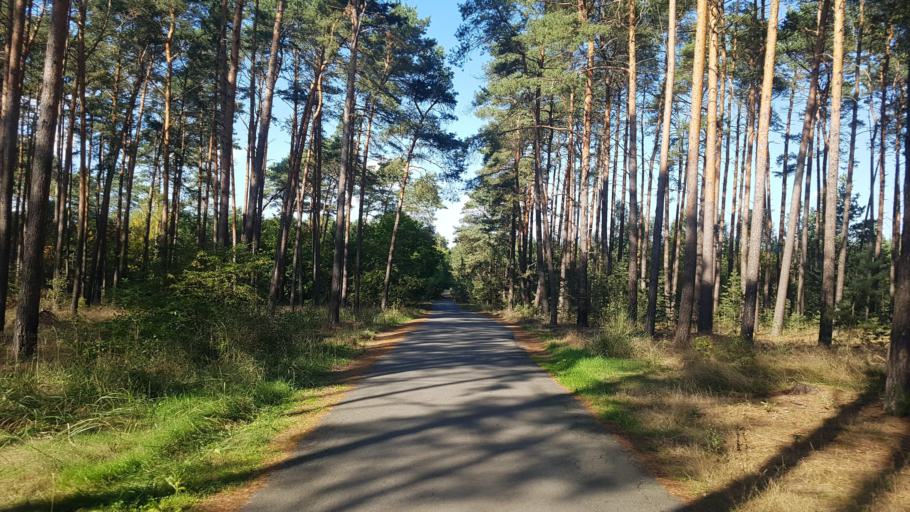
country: DE
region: Brandenburg
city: Ihlow
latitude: 51.8602
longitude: 13.2596
